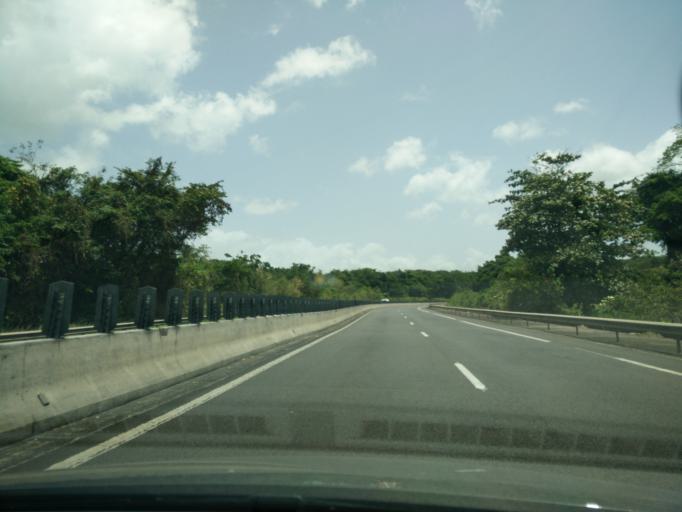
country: GP
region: Guadeloupe
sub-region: Guadeloupe
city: Les Abymes
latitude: 16.2742
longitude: -61.5337
